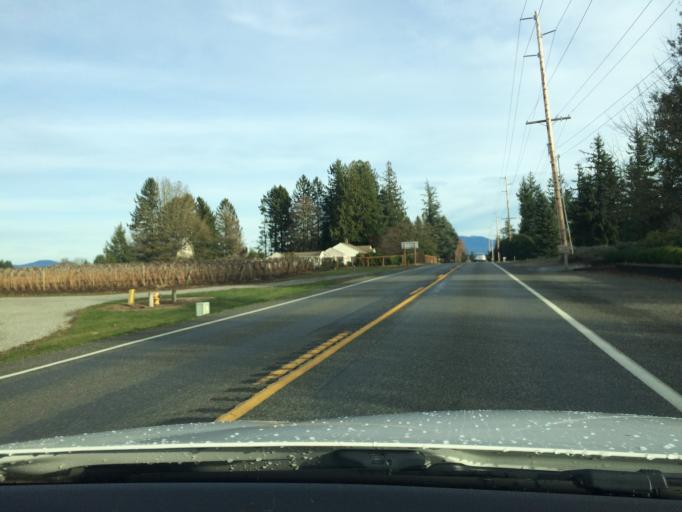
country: US
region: Washington
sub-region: Whatcom County
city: Lynden
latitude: 48.9641
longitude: -122.4158
